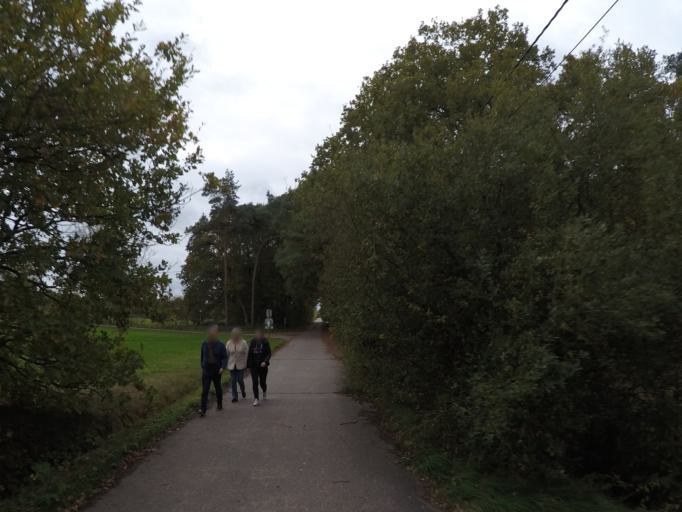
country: BE
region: Flanders
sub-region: Provincie Antwerpen
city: Zandhoven
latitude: 51.2512
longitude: 4.6696
